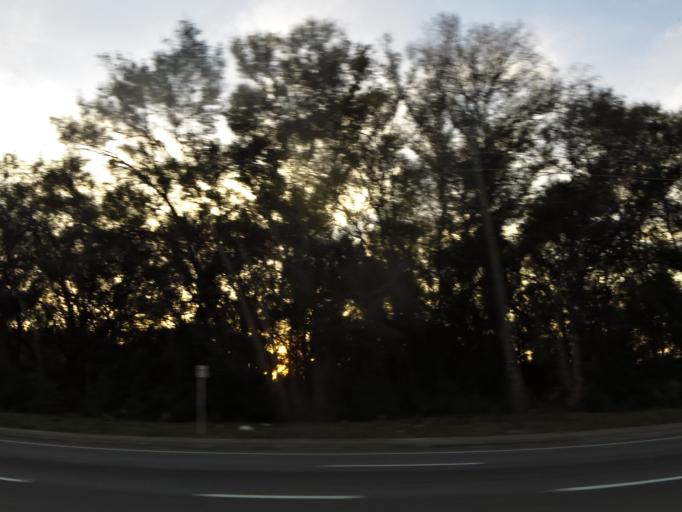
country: US
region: Florida
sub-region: Volusia County
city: North DeLand
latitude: 29.0658
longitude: -81.3046
